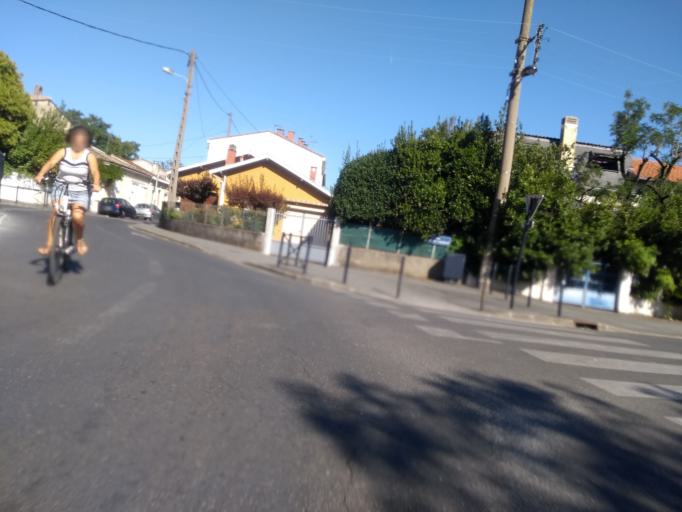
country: FR
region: Aquitaine
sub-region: Departement de la Gironde
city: Merignac
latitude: 44.8471
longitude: -0.6134
